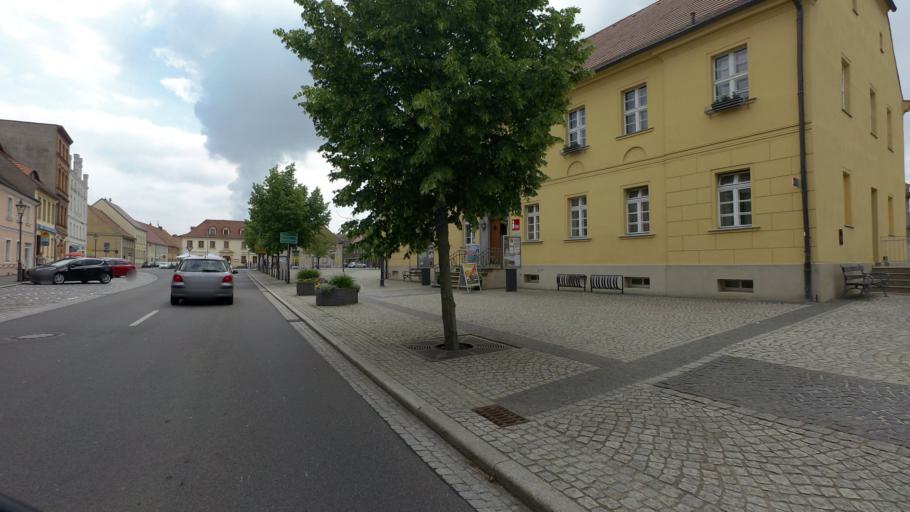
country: DE
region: Brandenburg
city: Peitz
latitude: 51.8589
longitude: 14.4106
